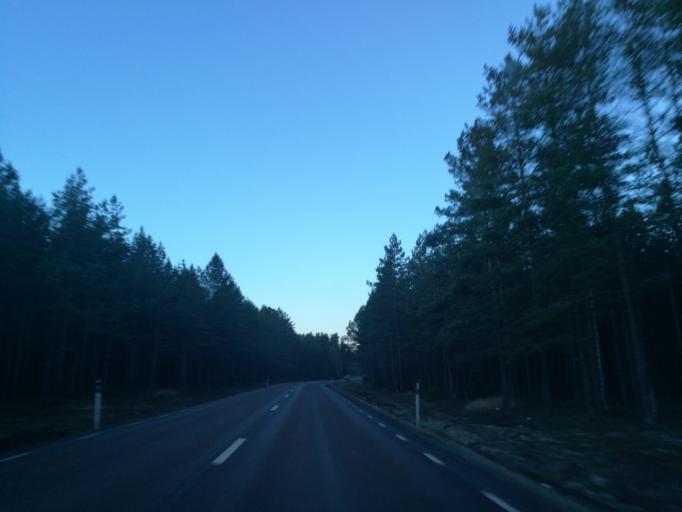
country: SE
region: Vaermland
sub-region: Eda Kommun
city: Charlottenberg
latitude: 59.9055
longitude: 12.2766
